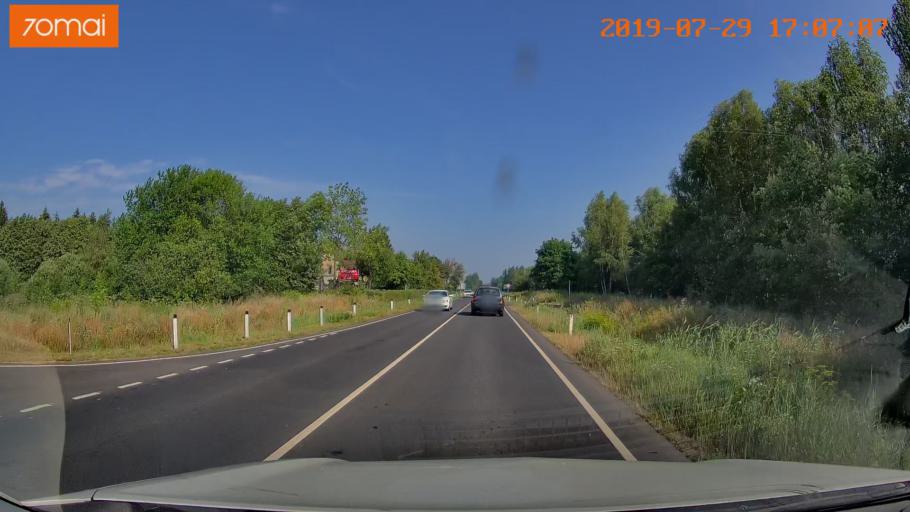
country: RU
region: Kaliningrad
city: Vzmorye
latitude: 54.8182
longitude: 20.3175
